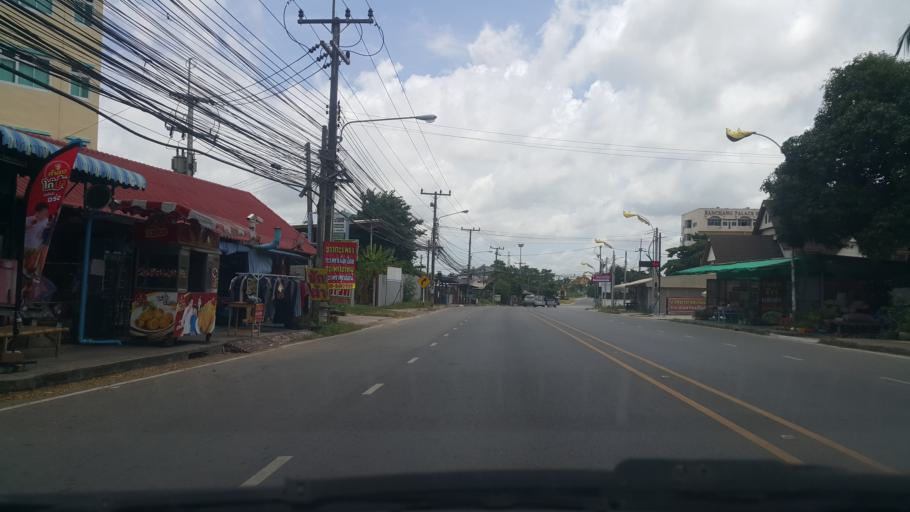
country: TH
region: Rayong
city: Ban Chang
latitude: 12.7342
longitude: 101.0474
